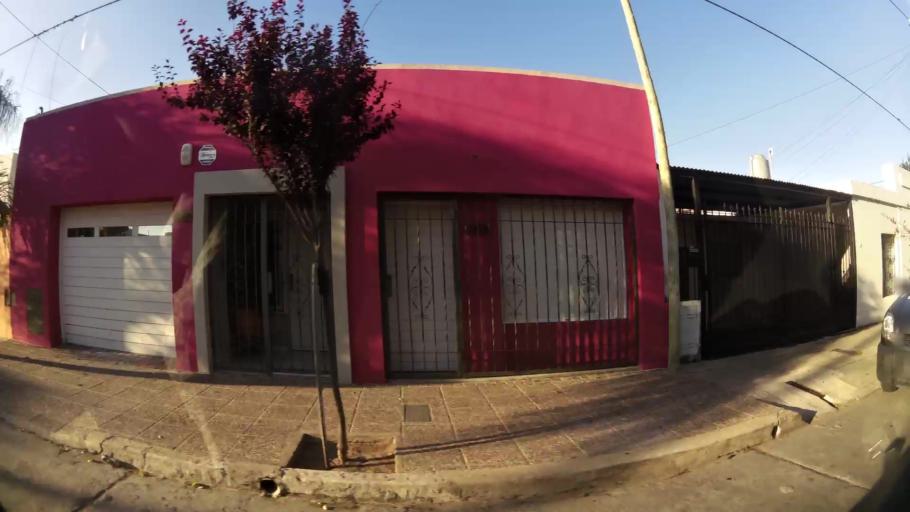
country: AR
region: Cordoba
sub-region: Departamento de Capital
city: Cordoba
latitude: -31.3740
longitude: -64.2051
